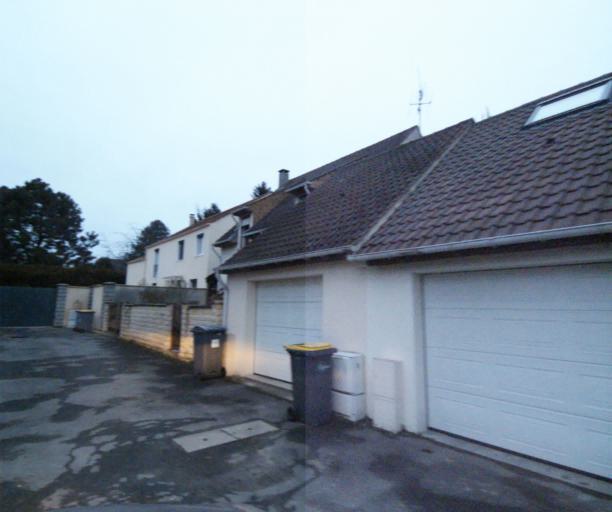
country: FR
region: Ile-de-France
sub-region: Departement de Seine-et-Marne
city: Longperrier
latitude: 49.0558
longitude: 2.6680
